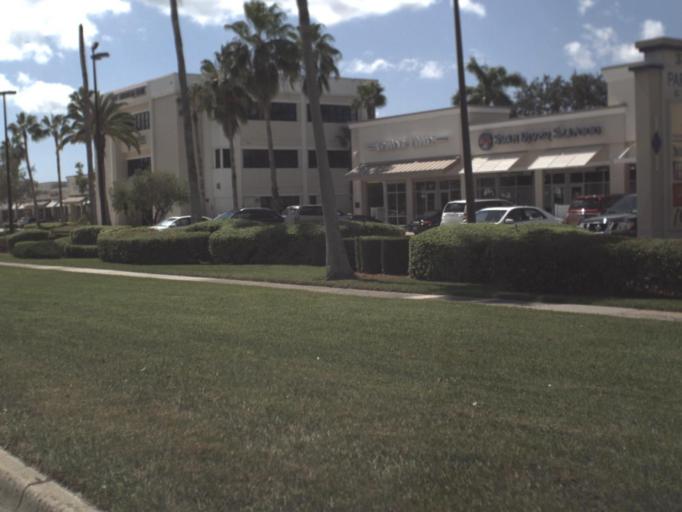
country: US
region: Florida
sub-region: Collier County
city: Pine Ridge
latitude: 26.1917
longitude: -81.8002
